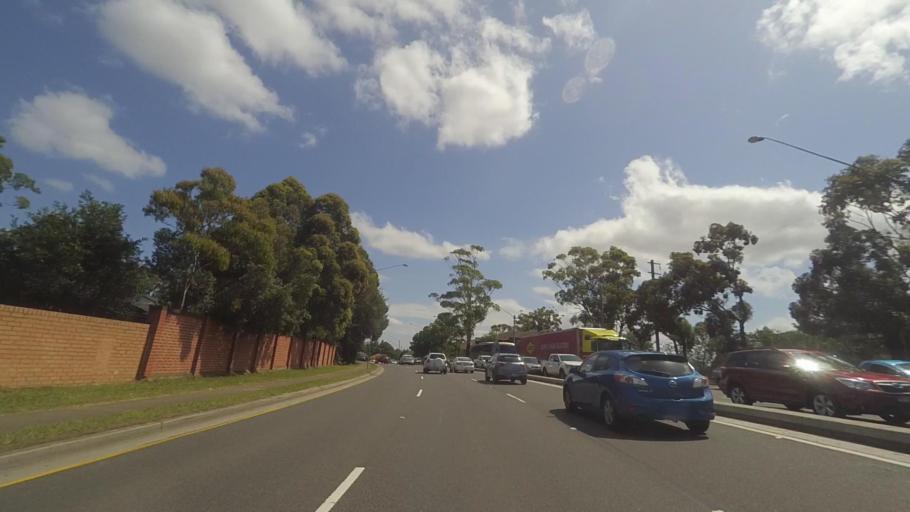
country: AU
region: New South Wales
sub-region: Hornsby Shire
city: Pennant Hills
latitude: -33.7333
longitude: 151.0774
